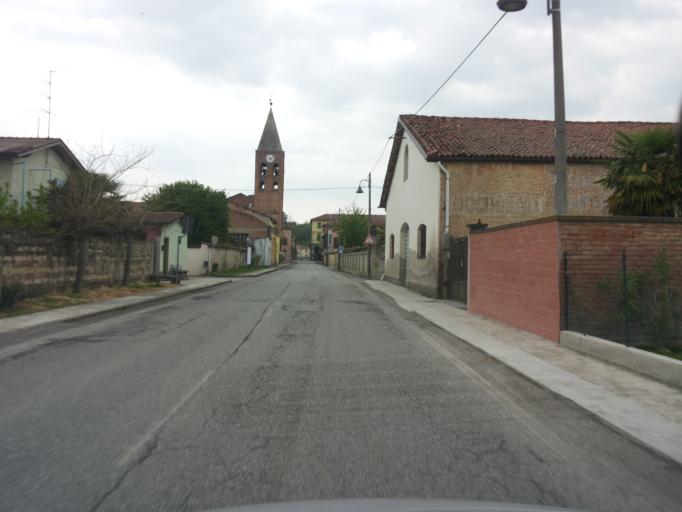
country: IT
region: Piedmont
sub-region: Provincia di Alessandria
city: Occimiano
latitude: 45.0593
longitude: 8.5091
